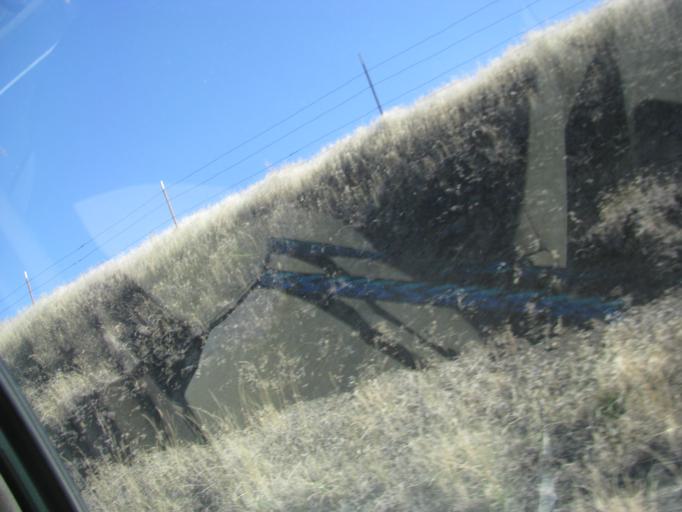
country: US
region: Washington
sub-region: Asotin County
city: Asotin
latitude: 46.3255
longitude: -117.0582
